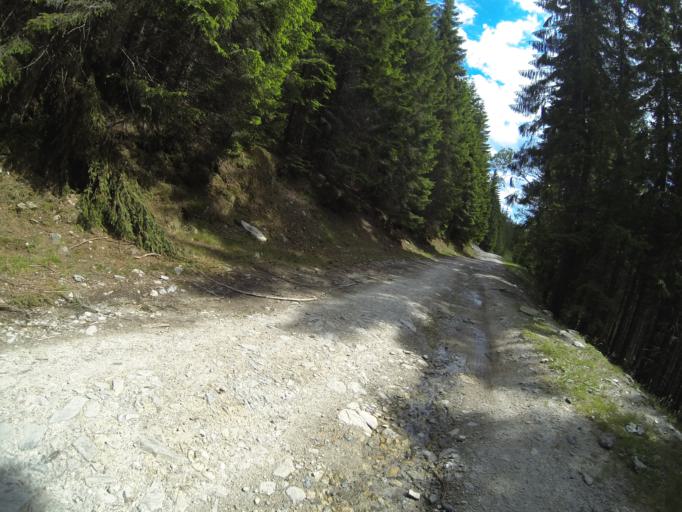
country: RO
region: Gorj
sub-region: Comuna Polovragi
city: Polovragi
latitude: 45.3403
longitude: 23.7956
